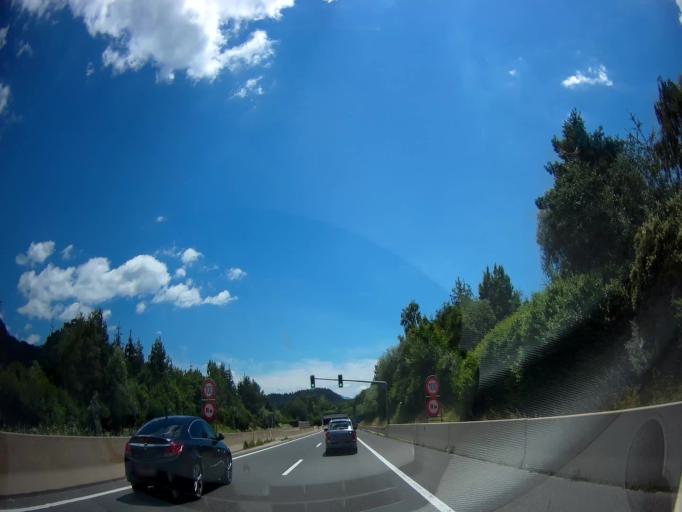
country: AT
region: Carinthia
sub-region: Villach Stadt
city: Villach
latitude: 46.6434
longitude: 13.8847
